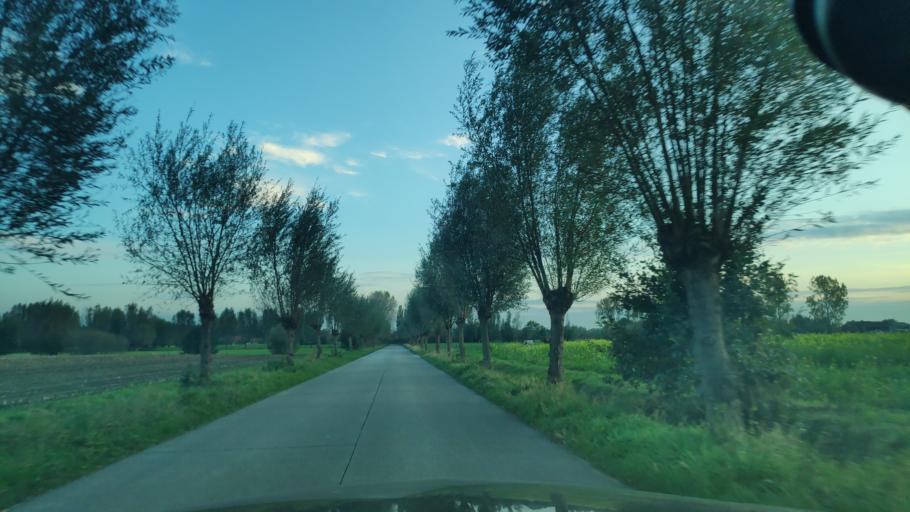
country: BE
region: Flanders
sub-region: Provincie Oost-Vlaanderen
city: Aalter
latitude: 51.1096
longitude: 3.4992
